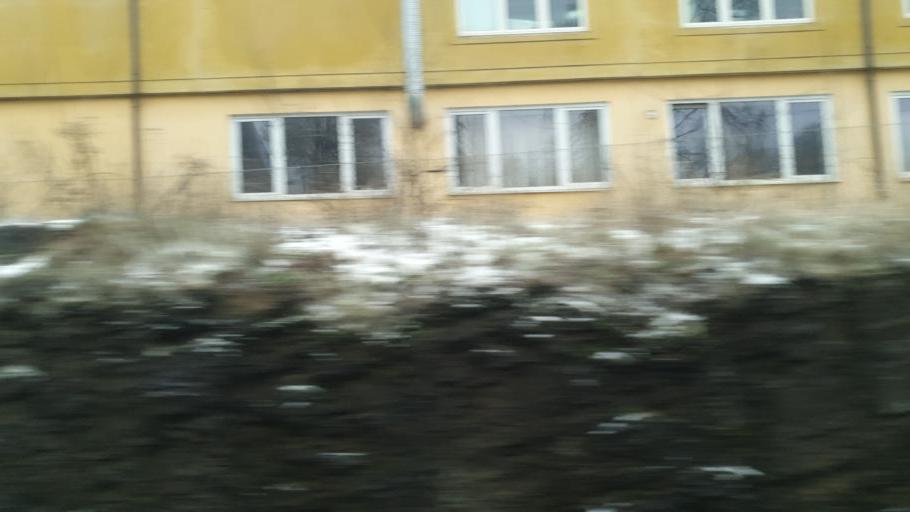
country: NO
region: Oslo
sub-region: Oslo
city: Oslo
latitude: 59.9082
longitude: 10.7986
